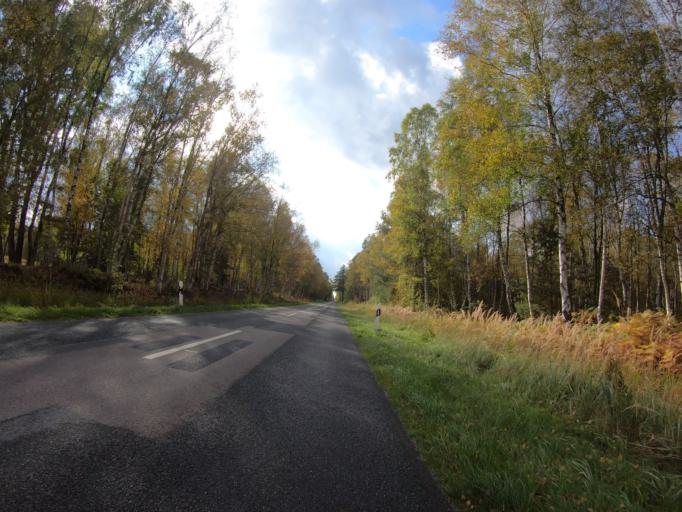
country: DE
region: Lower Saxony
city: Schoneworde
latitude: 52.5807
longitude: 10.6399
